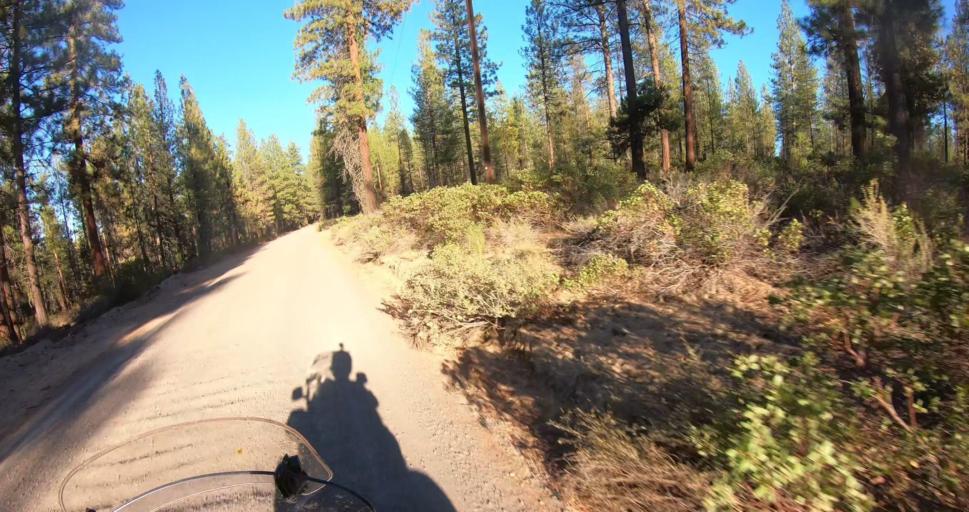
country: US
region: Oregon
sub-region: Deschutes County
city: La Pine
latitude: 43.7147
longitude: -121.3830
